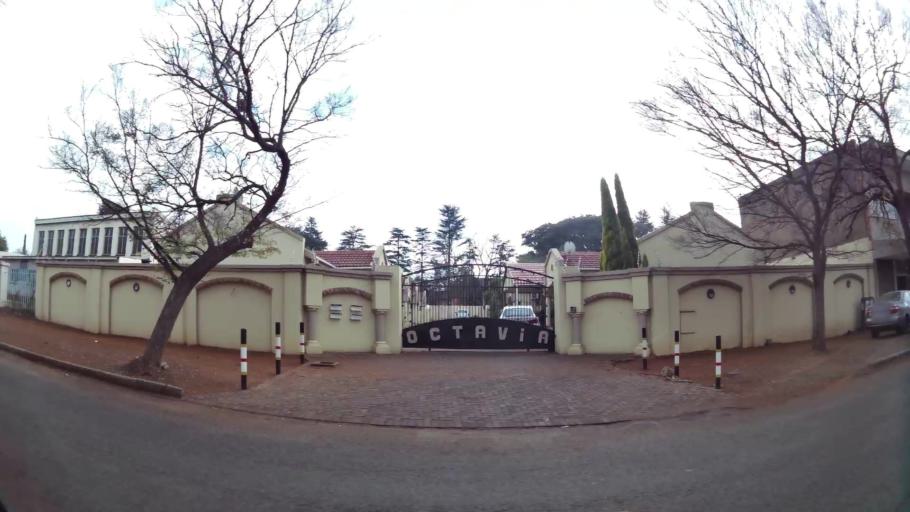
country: ZA
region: Gauteng
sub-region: Sedibeng District Municipality
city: Vanderbijlpark
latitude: -26.6966
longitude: 27.8163
